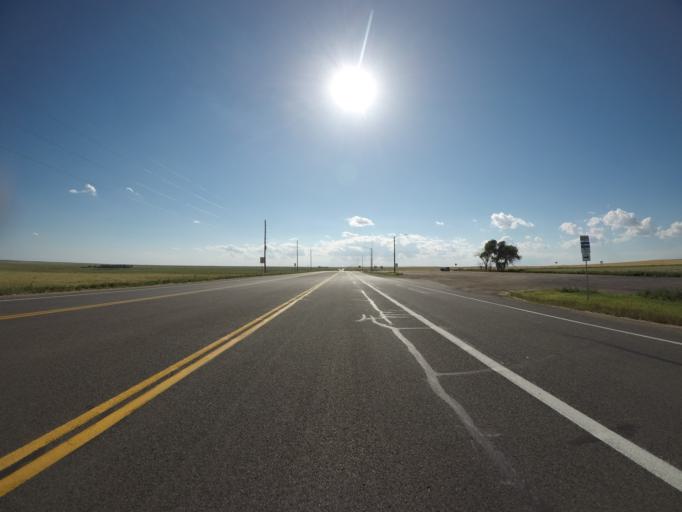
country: US
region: Colorado
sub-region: Morgan County
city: Brush
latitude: 40.6100
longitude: -103.6752
